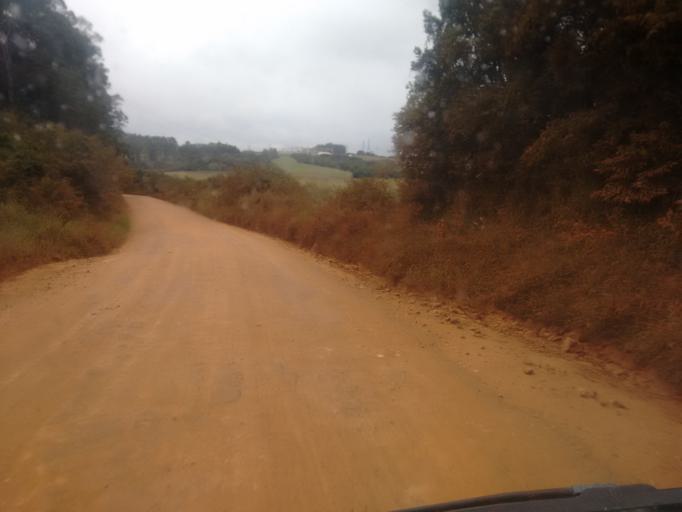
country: BR
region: Rio Grande do Sul
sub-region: Camaqua
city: Camaqua
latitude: -30.8185
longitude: -51.8133
